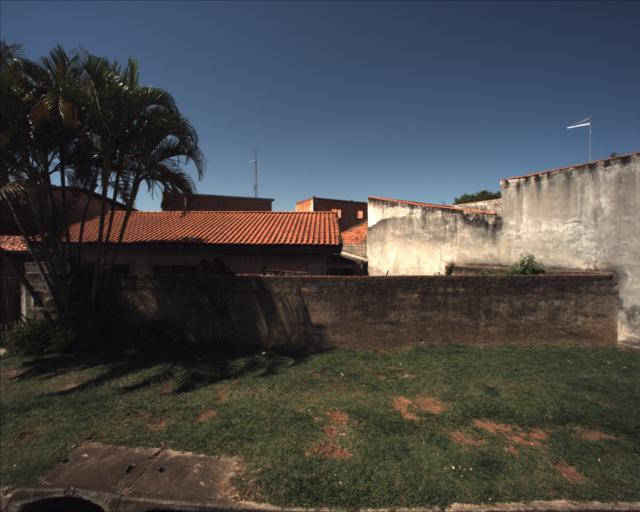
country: BR
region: Sao Paulo
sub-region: Sorocaba
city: Sorocaba
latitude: -23.4776
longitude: -47.4814
